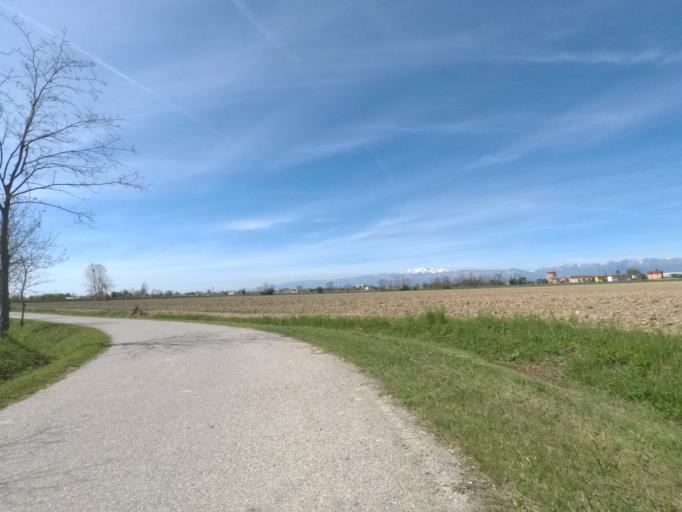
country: IT
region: Friuli Venezia Giulia
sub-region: Provincia di Pordenone
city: Casarsa della Delizia
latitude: 45.9523
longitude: 12.8596
